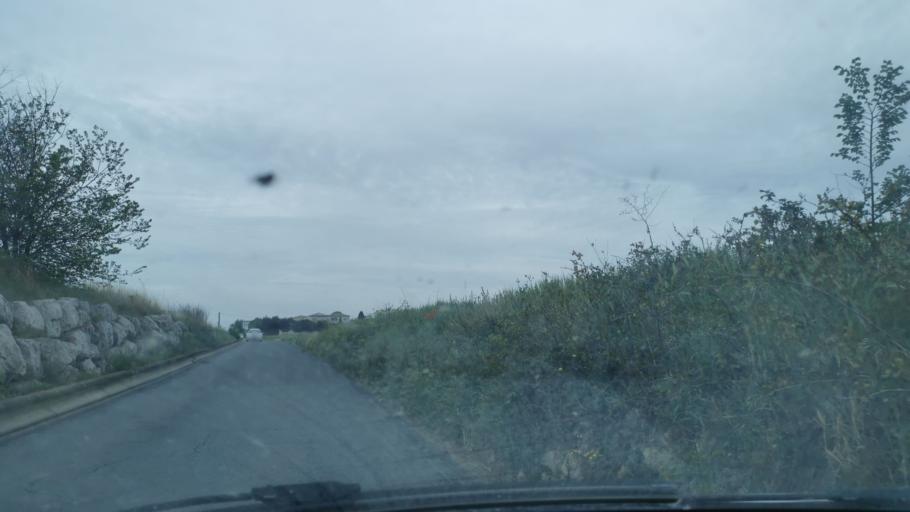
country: FR
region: Languedoc-Roussillon
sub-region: Departement de l'Herault
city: Saussan
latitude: 43.5678
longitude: 3.7811
